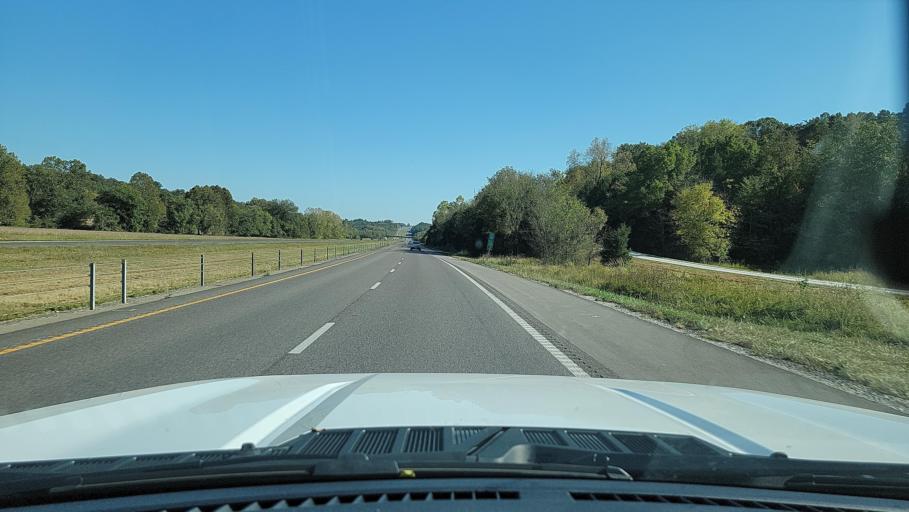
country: US
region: Missouri
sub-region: Sainte Genevieve County
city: Sainte Genevieve
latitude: 37.9002
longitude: -90.0669
